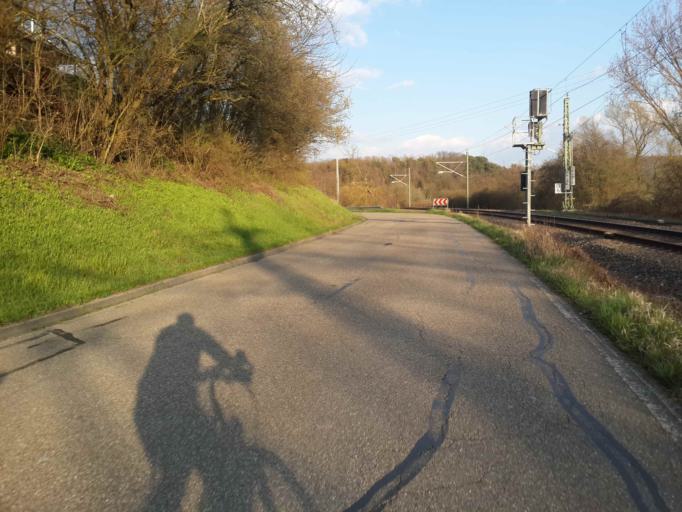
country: DE
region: Baden-Wuerttemberg
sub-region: Karlsruhe Region
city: Sinsheim
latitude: 49.2318
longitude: 8.9132
